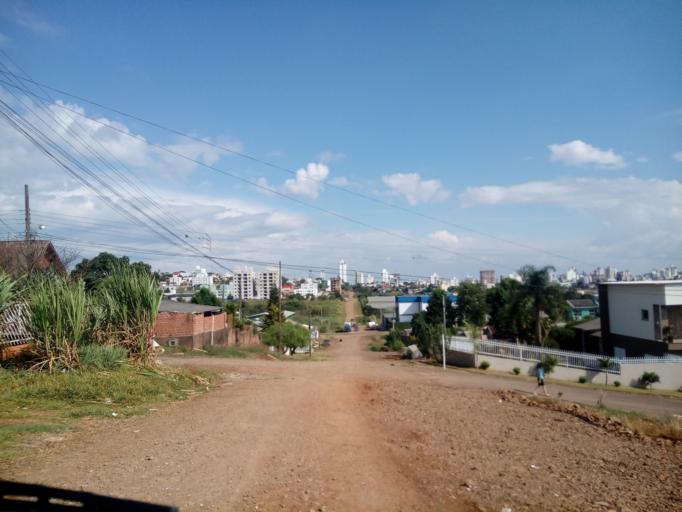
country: BR
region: Santa Catarina
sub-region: Chapeco
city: Chapeco
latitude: -27.0980
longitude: -52.5922
